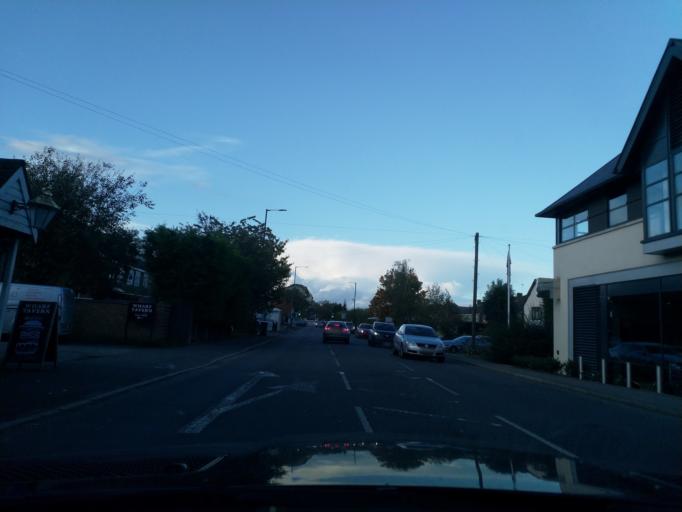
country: GB
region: England
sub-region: Solihull
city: Cheswick Green
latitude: 52.3507
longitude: -1.7773
